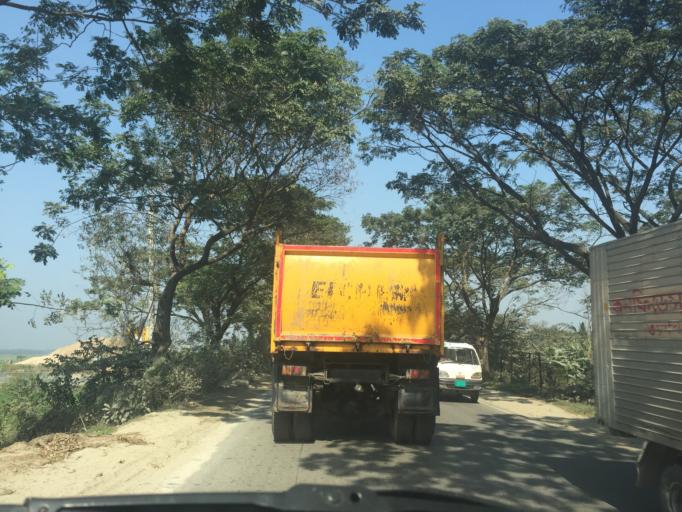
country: BD
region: Dhaka
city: Tungi
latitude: 23.8324
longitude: 90.3404
